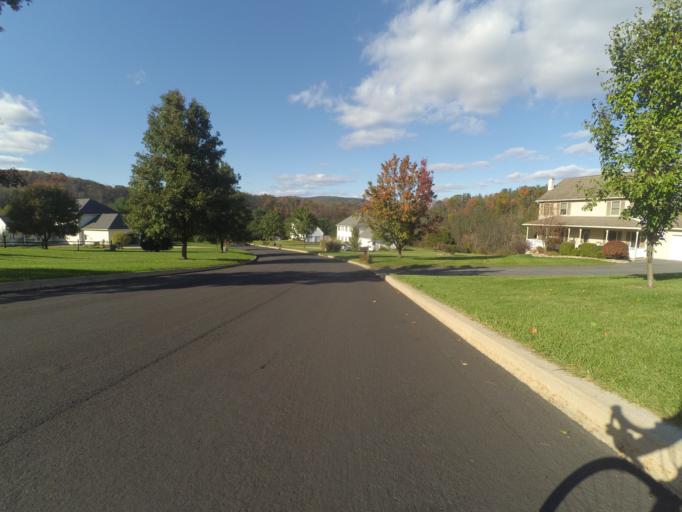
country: US
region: Pennsylvania
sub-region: Centre County
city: Bellefonte
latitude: 40.8868
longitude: -77.7924
